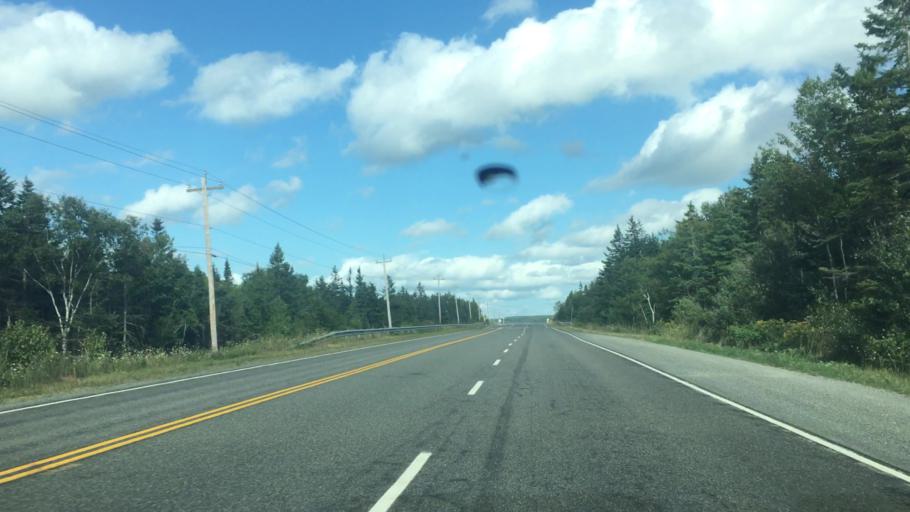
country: CA
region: Nova Scotia
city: Princeville
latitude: 45.8135
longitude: -60.6988
